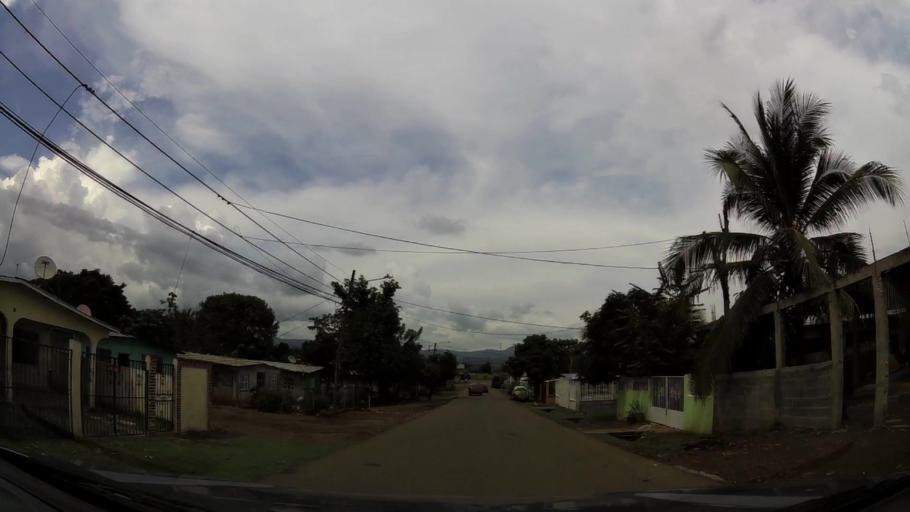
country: PA
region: Panama
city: Cabra Numero Uno
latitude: 9.1092
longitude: -79.3207
